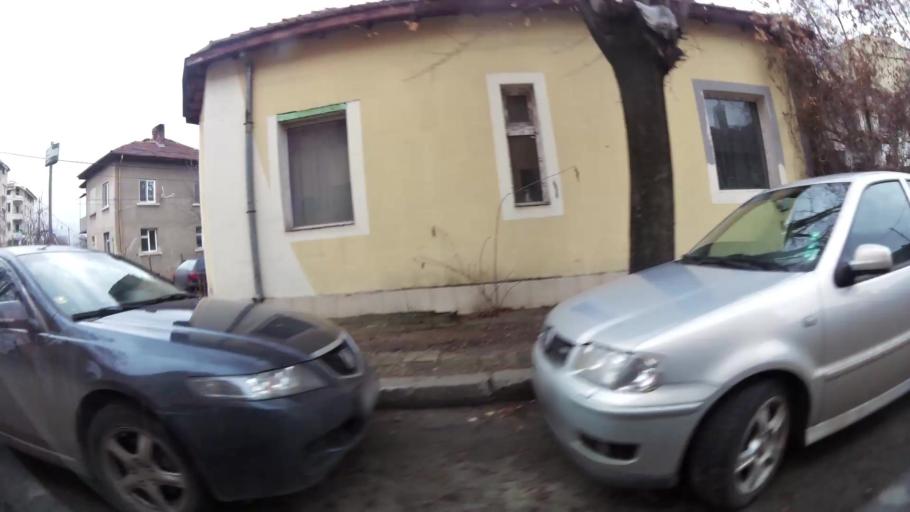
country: BG
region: Sofia-Capital
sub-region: Stolichna Obshtina
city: Sofia
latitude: 42.7203
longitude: 23.3076
